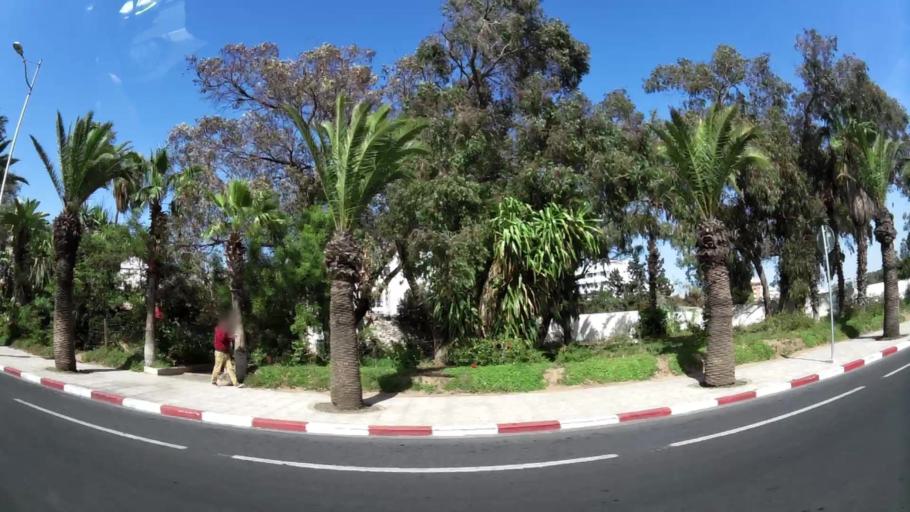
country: MA
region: Souss-Massa-Draa
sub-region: Agadir-Ida-ou-Tnan
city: Agadir
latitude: 30.4182
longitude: -9.6003
